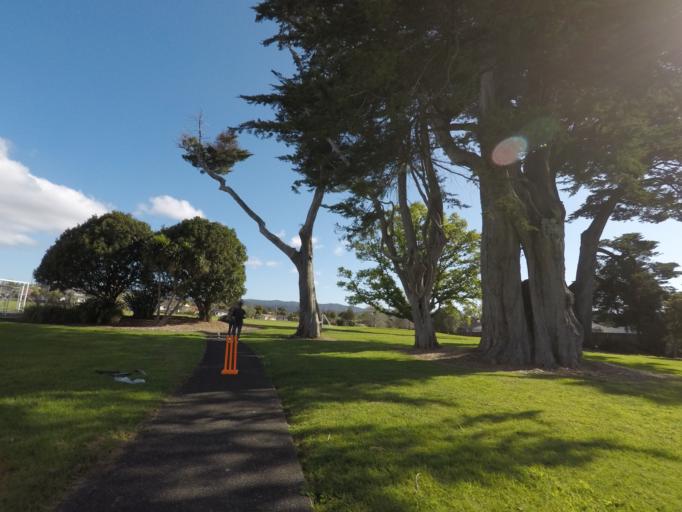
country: NZ
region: Auckland
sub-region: Auckland
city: Rosebank
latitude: -36.8588
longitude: 174.6042
